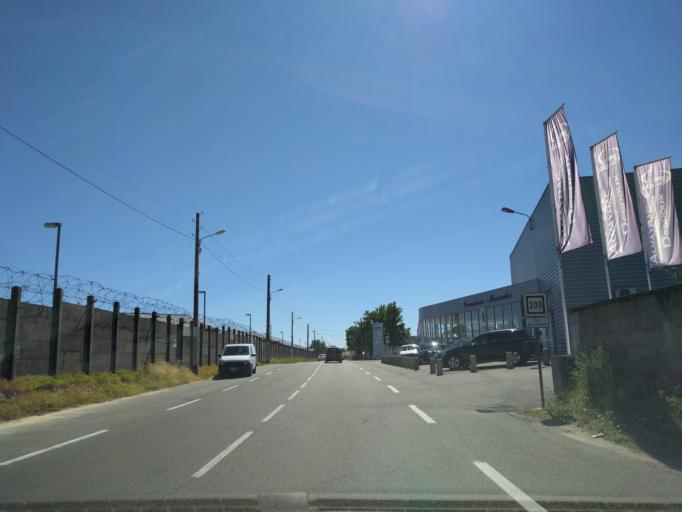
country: FR
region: Midi-Pyrenees
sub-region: Departement du Tarn-et-Garonne
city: Montauban
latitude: 44.0297
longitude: 1.3748
